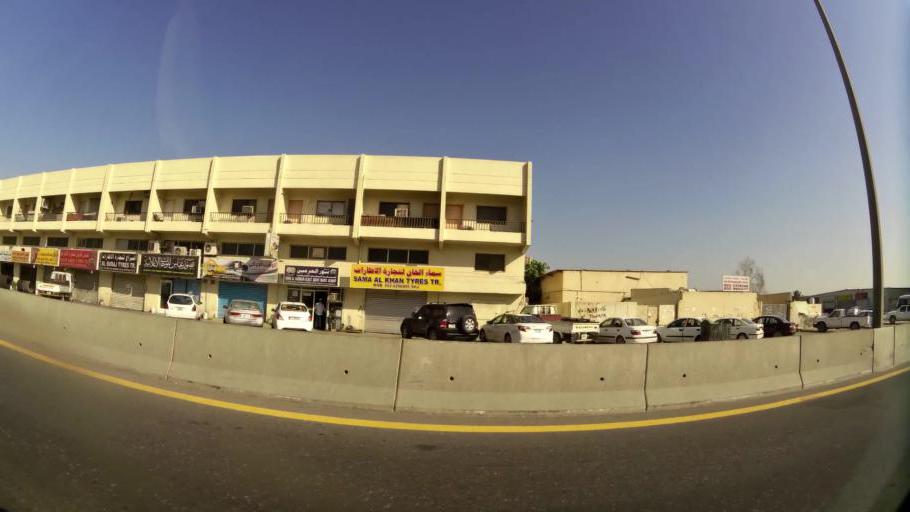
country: AE
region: Ash Shariqah
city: Sharjah
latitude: 25.3080
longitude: 55.4040
